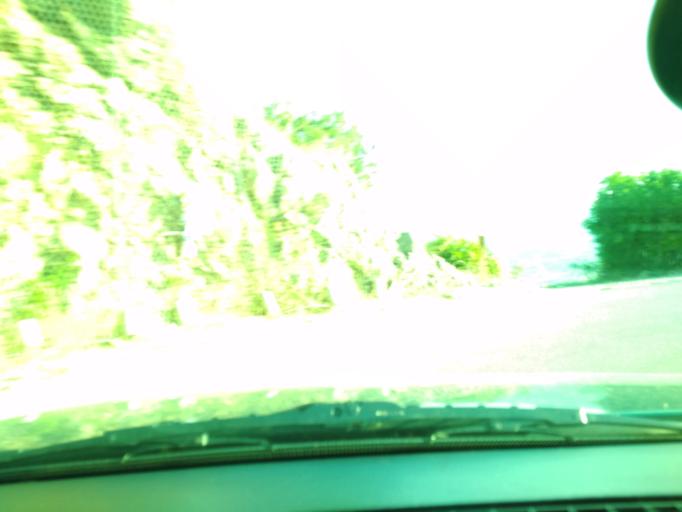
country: ME
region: Kotor
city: Kotor
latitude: 42.3951
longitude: 18.7596
